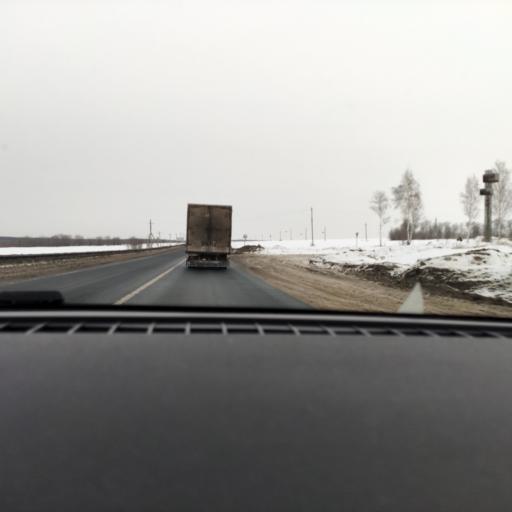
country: RU
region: Samara
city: Petra-Dubrava
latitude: 53.3058
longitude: 50.4579
